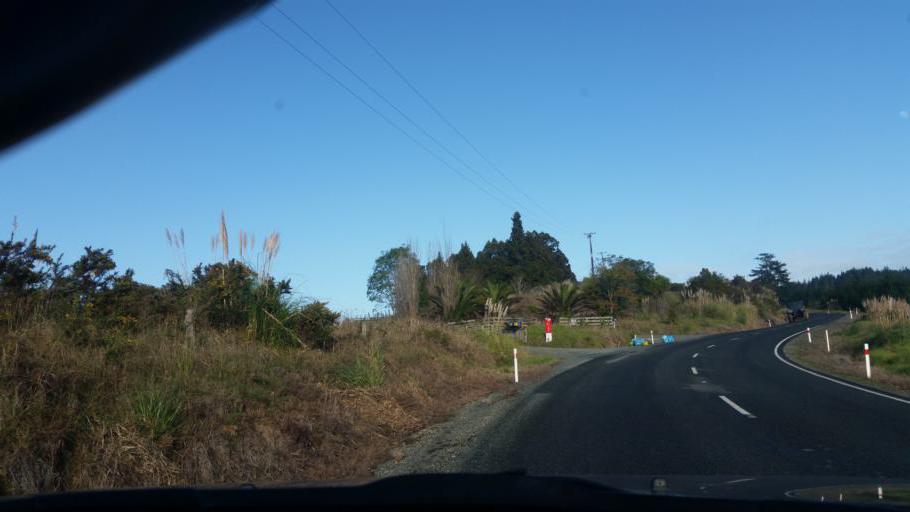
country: NZ
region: Auckland
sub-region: Auckland
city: Wellsford
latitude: -36.2211
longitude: 174.4613
